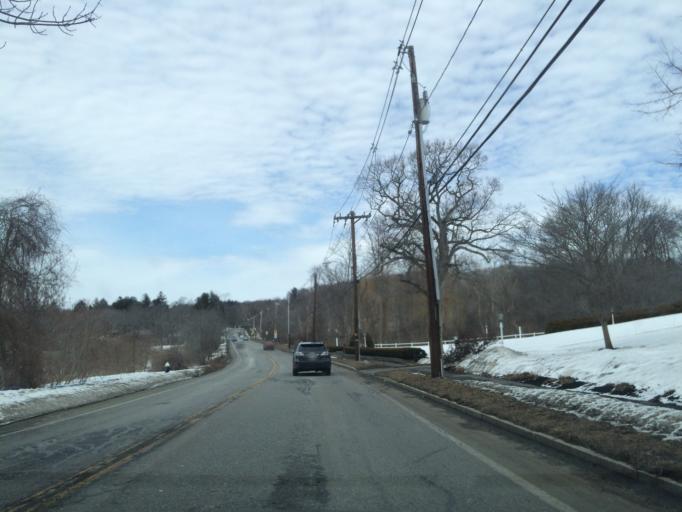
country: US
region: Massachusetts
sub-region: Middlesex County
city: Lexington
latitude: 42.4288
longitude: -71.2312
